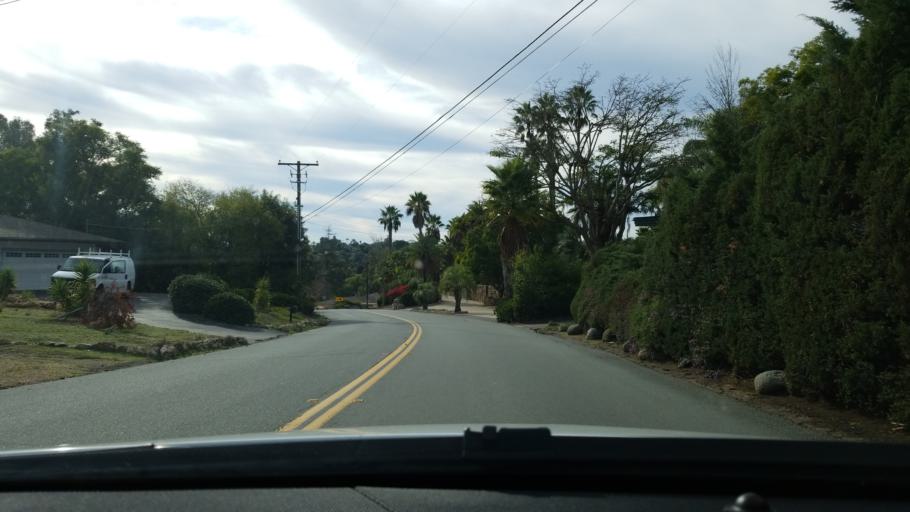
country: US
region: California
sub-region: San Diego County
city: Casa de Oro-Mount Helix
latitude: 32.7710
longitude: -116.9549
